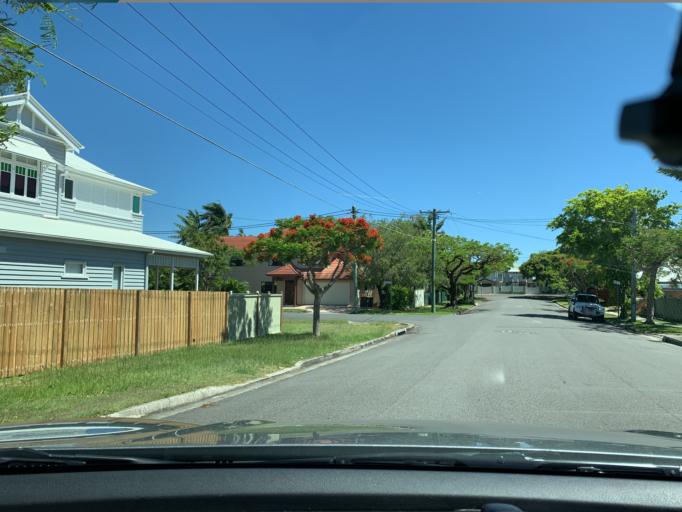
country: AU
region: Queensland
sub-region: Brisbane
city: Ascot
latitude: -27.4237
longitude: 153.0673
